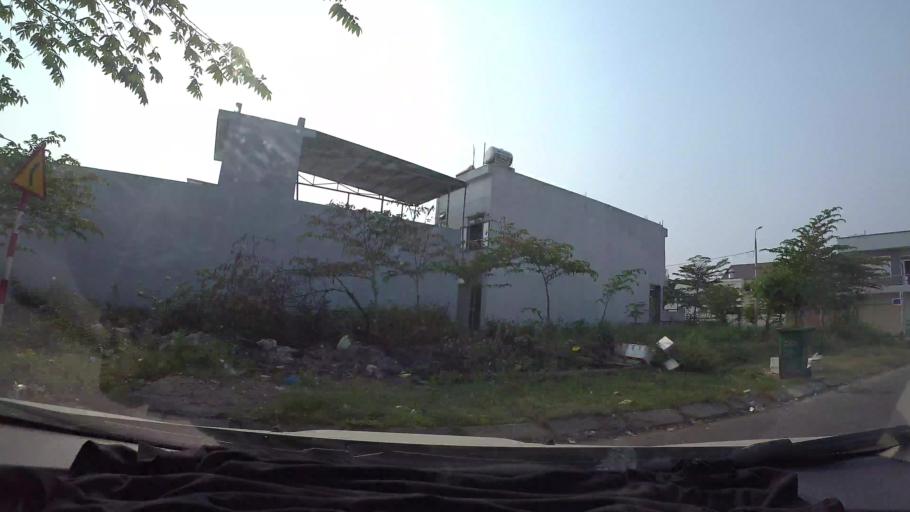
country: VN
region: Da Nang
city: Lien Chieu
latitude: 16.0514
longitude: 108.1682
